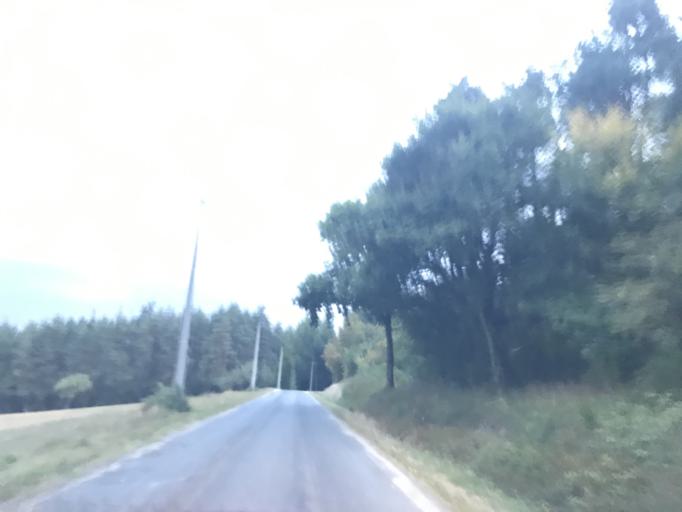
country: FR
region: Auvergne
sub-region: Departement du Puy-de-Dome
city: Escoutoux
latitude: 45.8013
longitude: 3.5673
